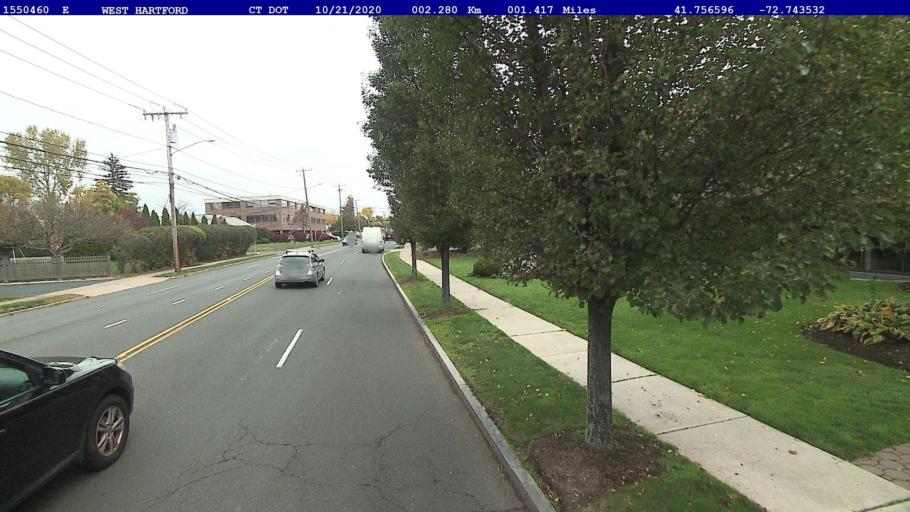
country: US
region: Connecticut
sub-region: Hartford County
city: West Hartford
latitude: 41.7566
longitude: -72.7435
